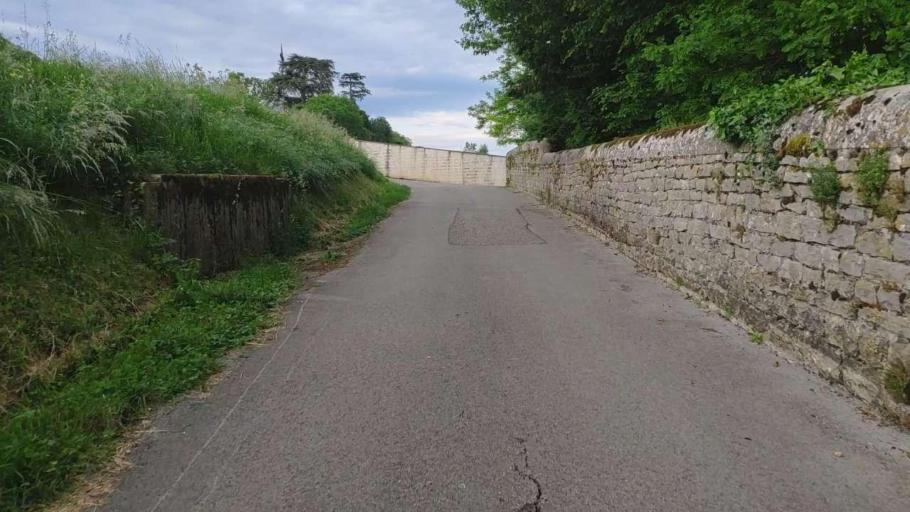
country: FR
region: Franche-Comte
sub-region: Departement du Jura
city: Perrigny
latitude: 46.7159
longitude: 5.5972
